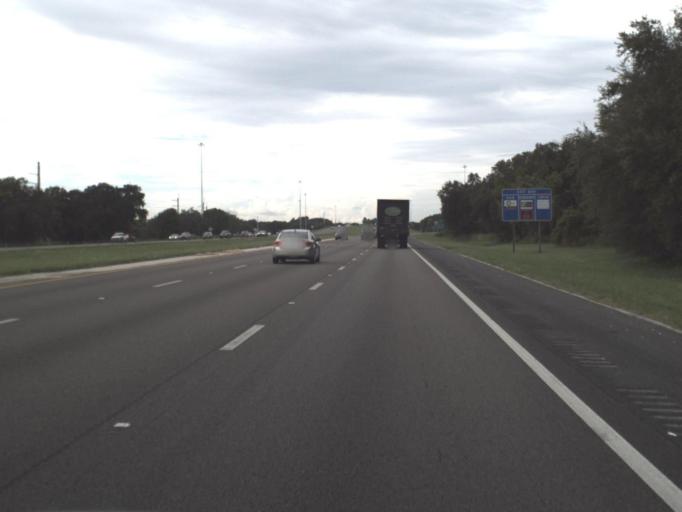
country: US
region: Florida
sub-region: Sarasota County
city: Lake Sarasota
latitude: 27.2778
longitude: -82.4491
